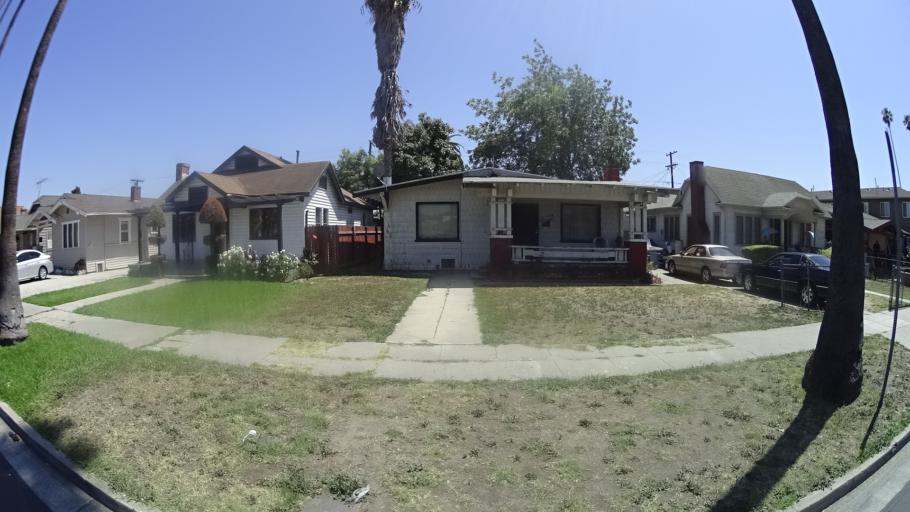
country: US
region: California
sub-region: Los Angeles County
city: View Park-Windsor Hills
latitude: 33.9968
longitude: -118.3061
